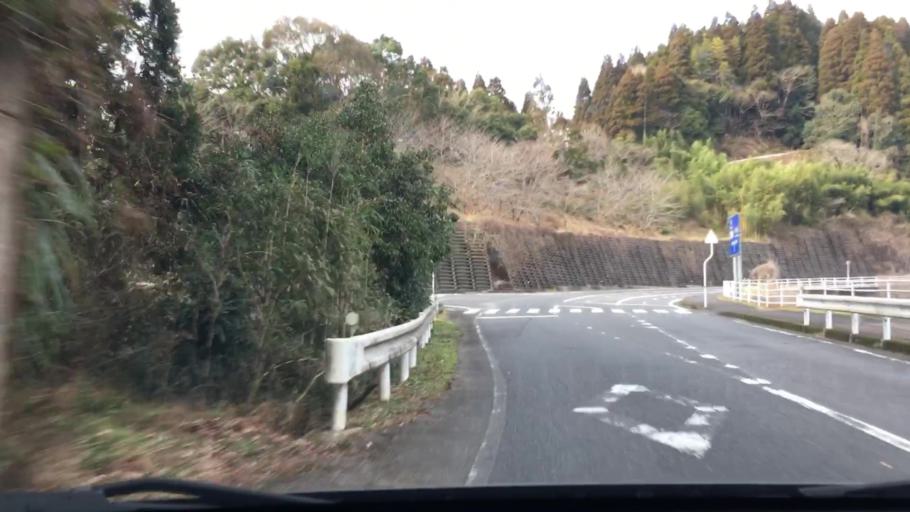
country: JP
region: Miyazaki
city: Kushima
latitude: 31.5460
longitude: 131.2420
